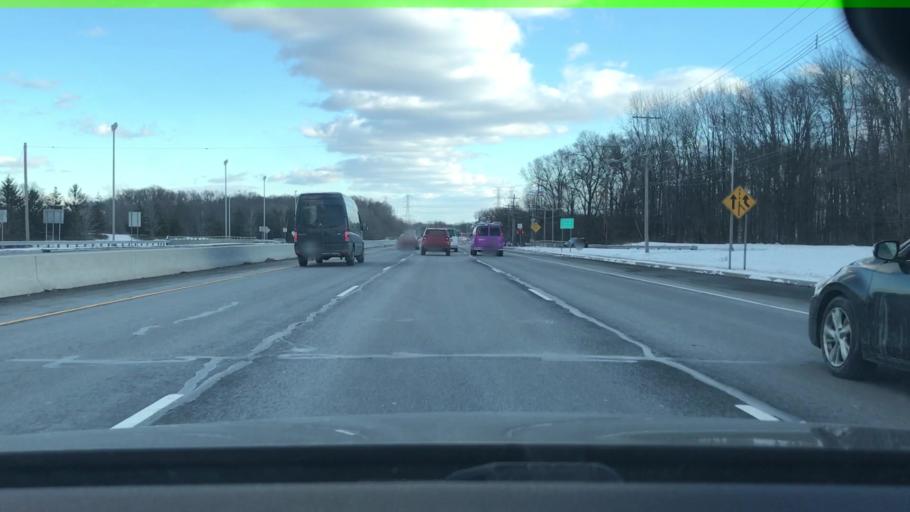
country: US
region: New Jersey
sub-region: Morris County
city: Parsippany
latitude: 40.8388
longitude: -74.4525
